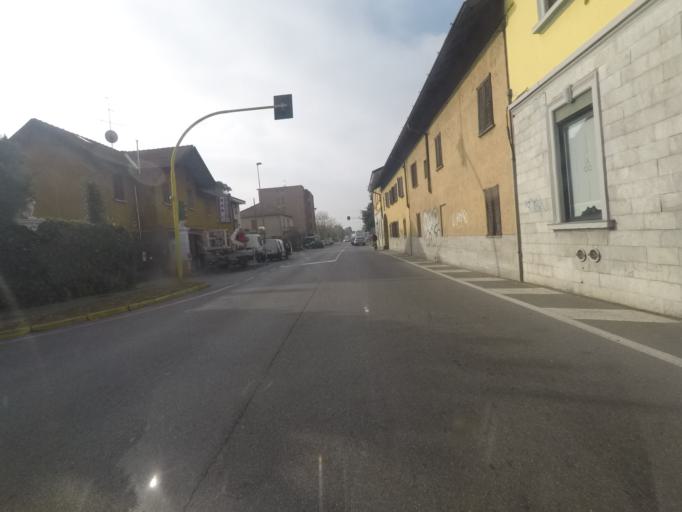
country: IT
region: Lombardy
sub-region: Provincia di Monza e Brianza
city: Brugherio
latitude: 45.5484
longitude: 9.2938
